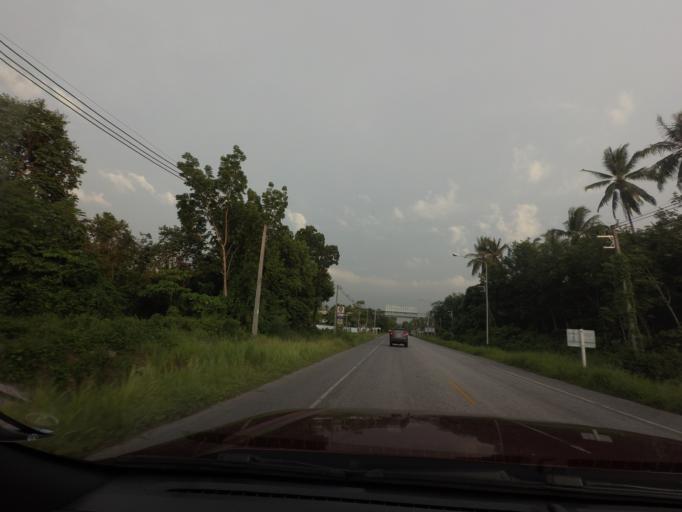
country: TH
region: Pattani
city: Mae Lan
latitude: 6.6002
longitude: 101.1940
